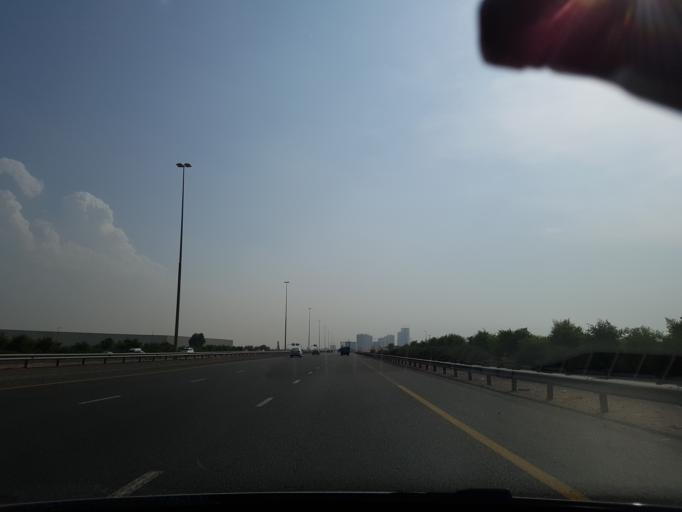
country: AE
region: Umm al Qaywayn
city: Umm al Qaywayn
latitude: 25.4233
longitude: 55.5914
